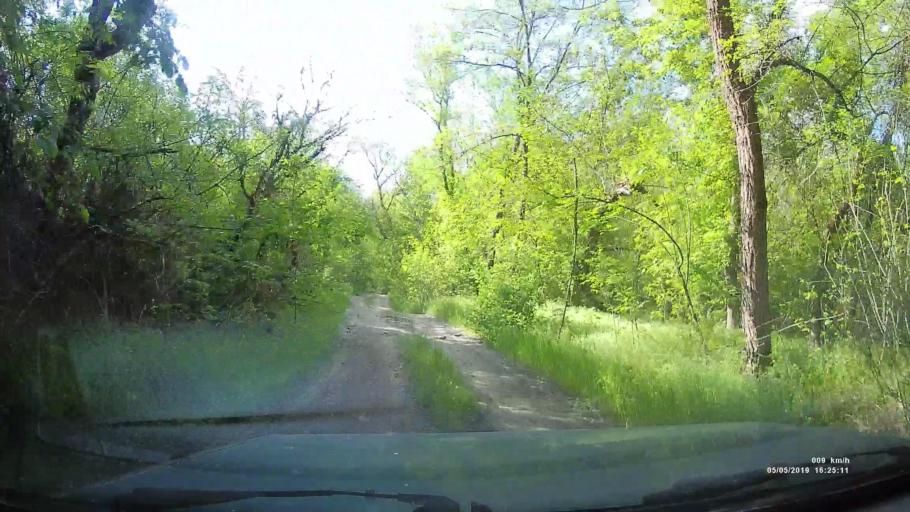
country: RU
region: Rostov
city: Konstantinovsk
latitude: 47.7611
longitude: 41.0238
